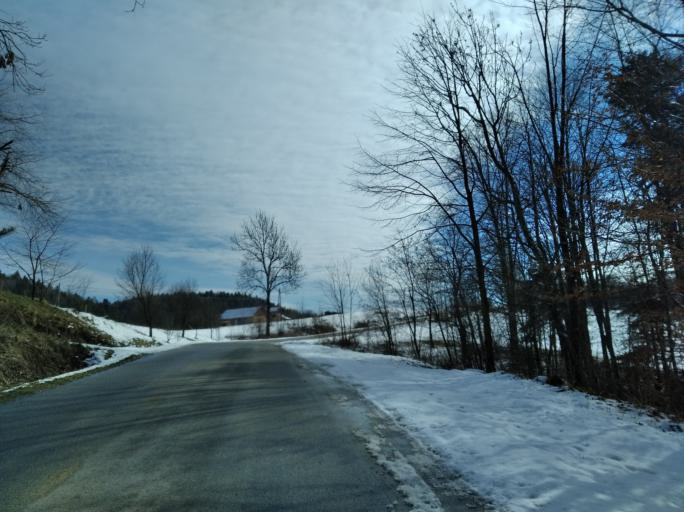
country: PL
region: Subcarpathian Voivodeship
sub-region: Powiat brzozowski
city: Jablonica Polska
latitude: 49.7294
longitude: 21.8981
